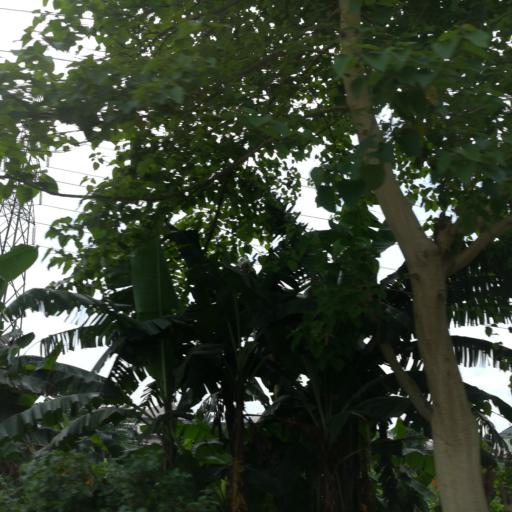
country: NG
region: Rivers
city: Port Harcourt
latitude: 4.8659
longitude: 7.0183
